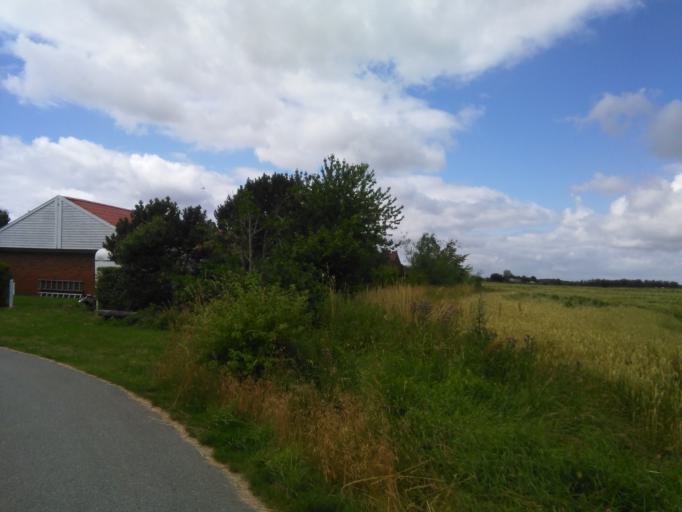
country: DK
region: Central Jutland
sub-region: Arhus Kommune
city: Marslet
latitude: 56.0772
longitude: 10.1514
